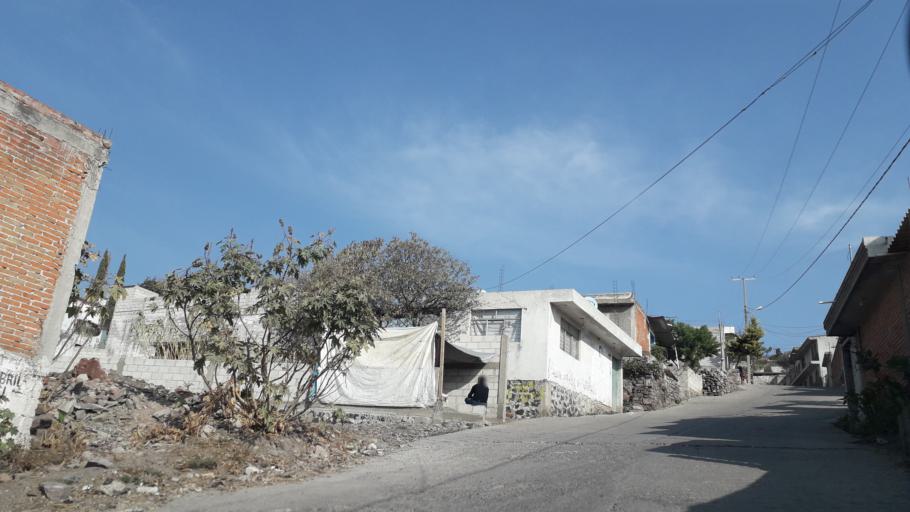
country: MX
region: Puebla
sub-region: Puebla
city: San Andres Azumiatla
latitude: 18.9019
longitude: -98.2550
